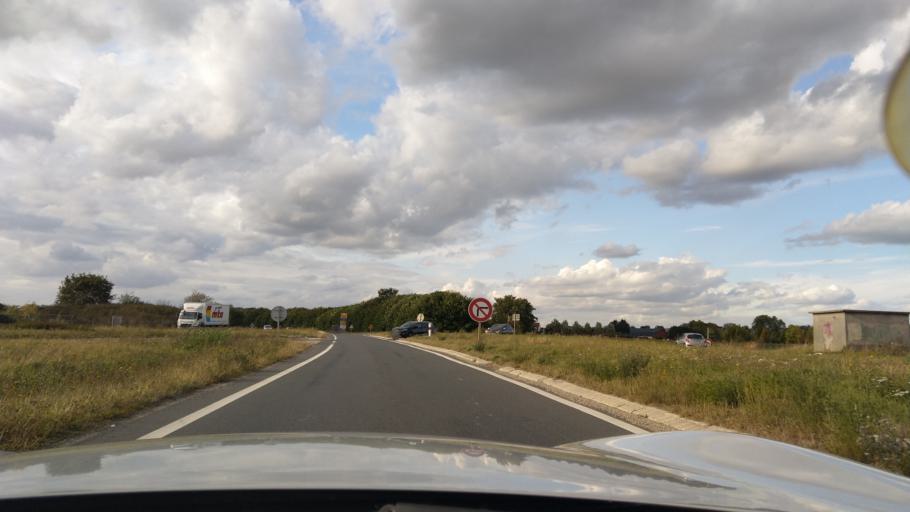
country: FR
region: Ile-de-France
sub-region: Departement de Seine-et-Marne
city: Moussy-le-Neuf
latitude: 49.0261
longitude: 2.5836
